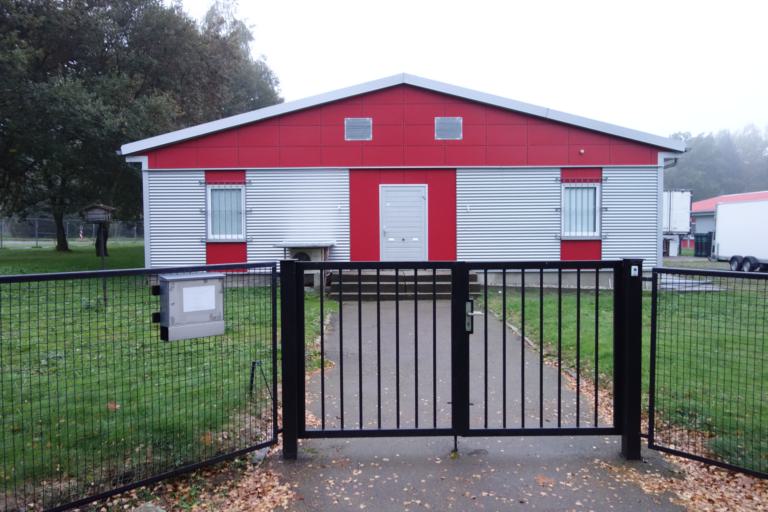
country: DE
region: Saxony
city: Freiberg
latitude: 50.9065
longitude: 13.3139
